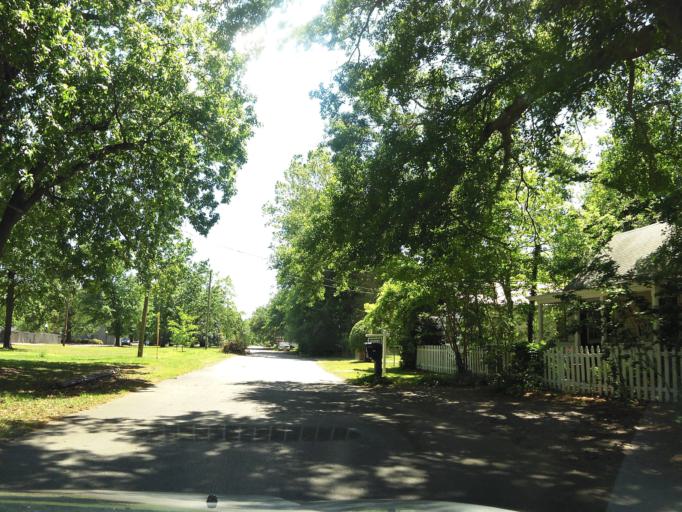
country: US
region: South Carolina
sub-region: Aiken County
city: Aiken
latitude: 33.5590
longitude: -81.7107
